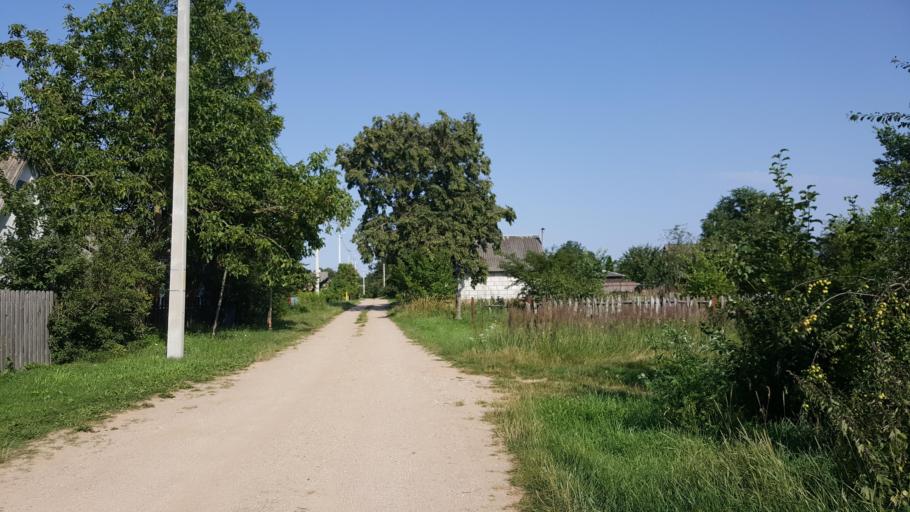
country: BY
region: Brest
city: Zhabinka
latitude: 52.2380
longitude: 24.0109
